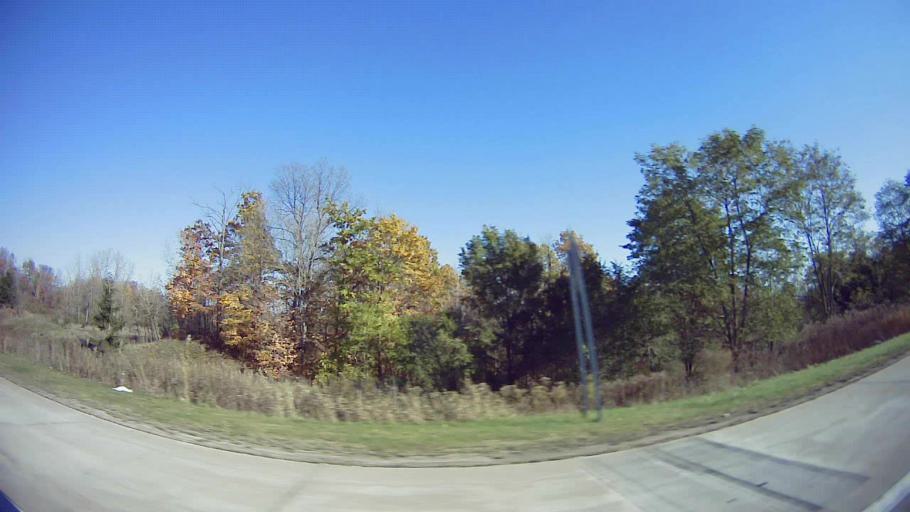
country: US
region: Michigan
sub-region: Oakland County
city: Walled Lake
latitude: 42.5240
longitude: -83.4453
